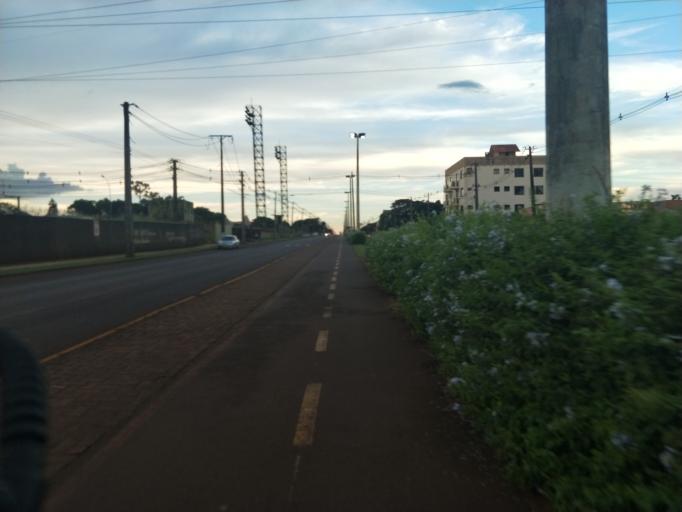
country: BR
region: Parana
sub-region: Marechal Candido Rondon
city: Marechal Candido Rondon
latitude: -24.5556
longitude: -54.0475
